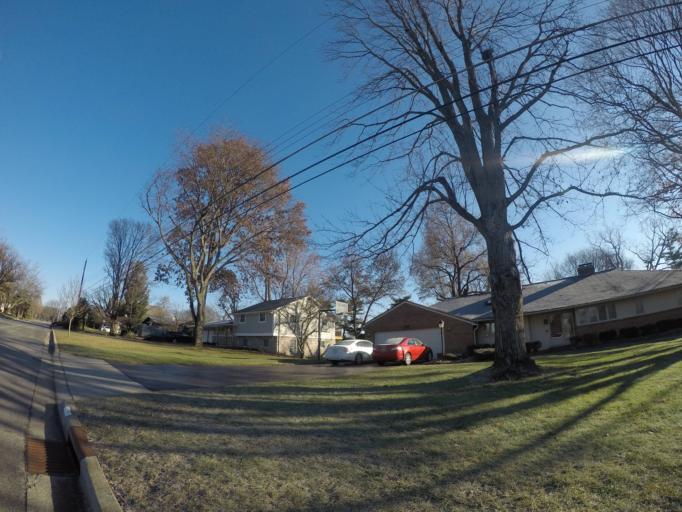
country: US
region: Ohio
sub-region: Franklin County
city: Upper Arlington
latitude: 40.0382
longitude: -83.0631
